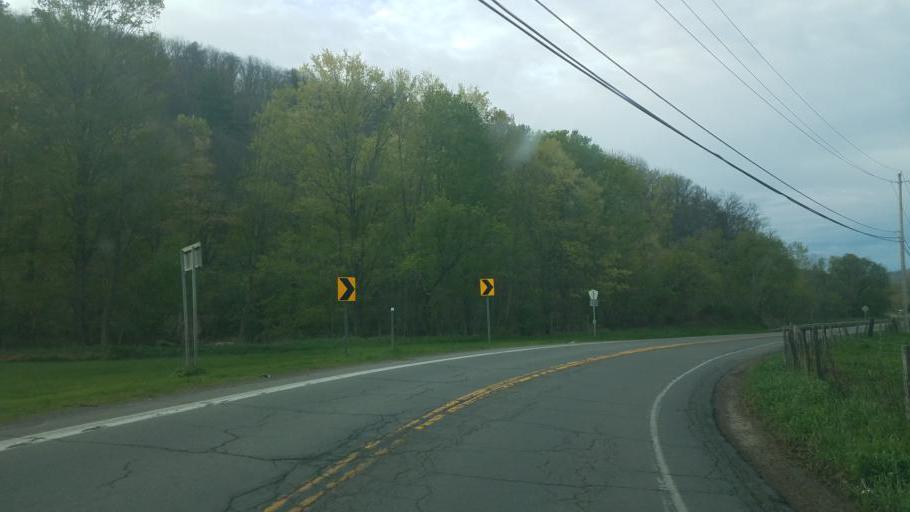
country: US
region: New York
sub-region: Steuben County
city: Canisteo
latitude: 42.2586
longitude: -77.5838
